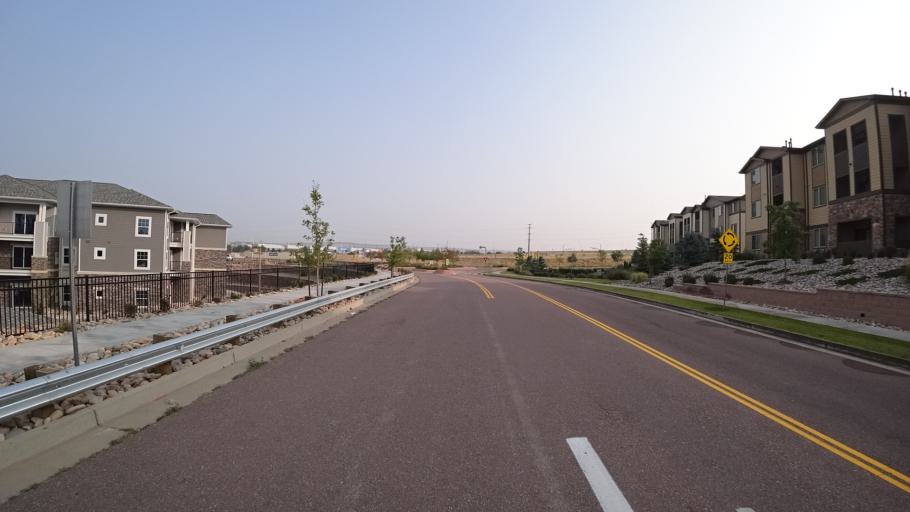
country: US
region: Colorado
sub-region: El Paso County
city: Black Forest
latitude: 38.9378
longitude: -104.7249
